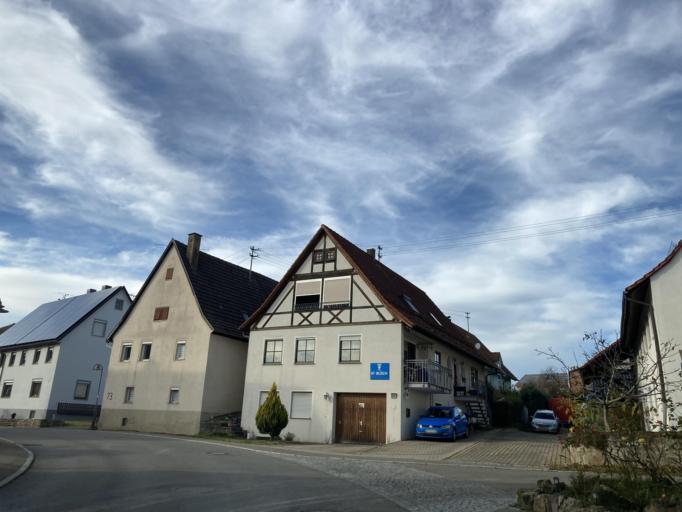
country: DE
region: Baden-Wuerttemberg
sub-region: Tuebingen Region
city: Haigerloch
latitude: 48.4312
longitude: 8.8182
